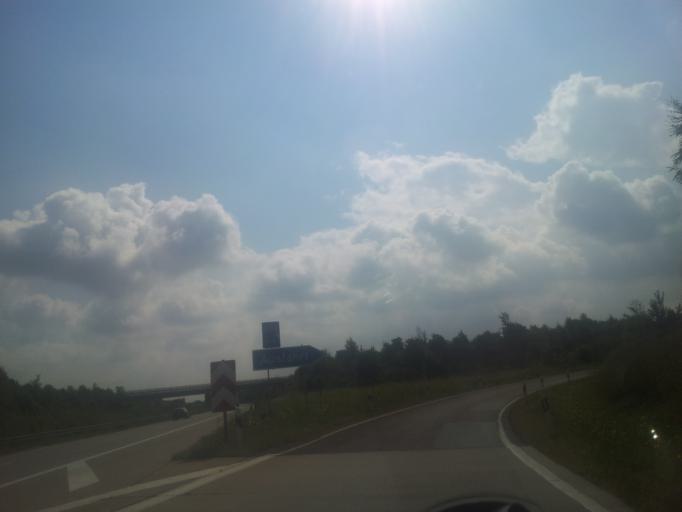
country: DE
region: Saxony-Anhalt
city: Trebitz
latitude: 51.5737
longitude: 11.9011
